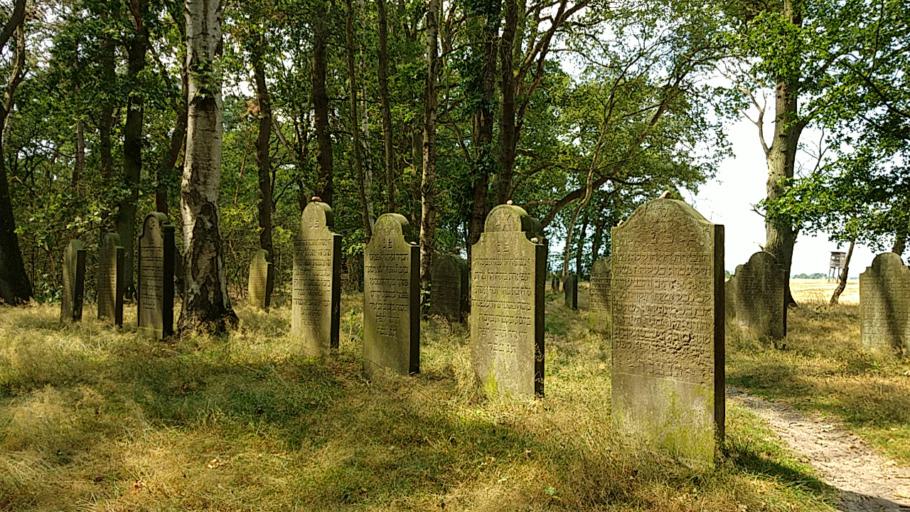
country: DE
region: Lower Saxony
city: Wunstorf
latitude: 52.4401
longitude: 9.3837
